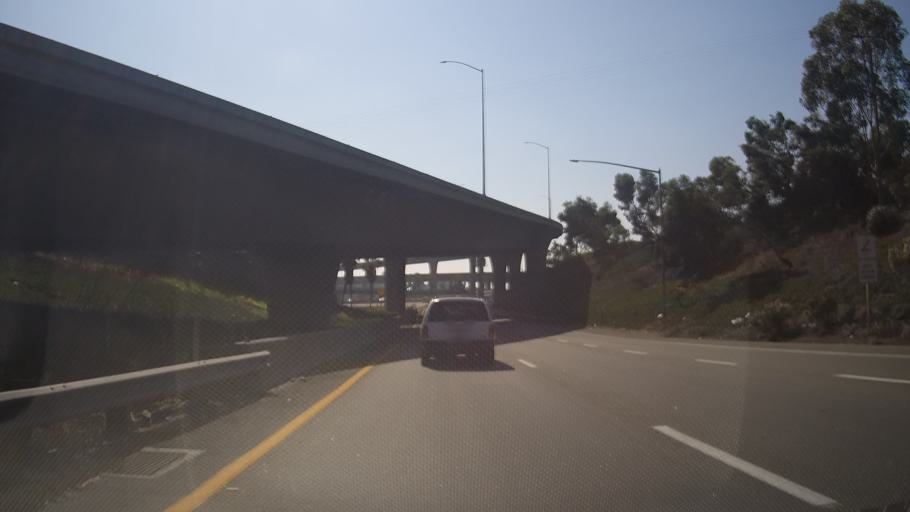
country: US
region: California
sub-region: San Diego County
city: Lemon Grove
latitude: 32.7505
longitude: -117.0166
